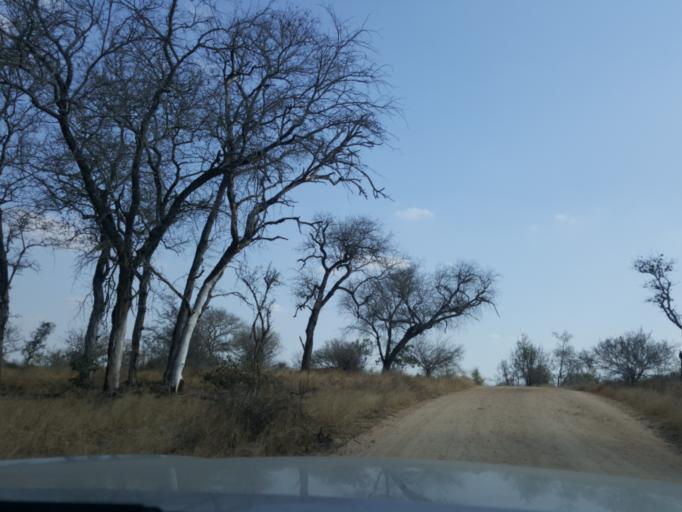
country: ZA
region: Mpumalanga
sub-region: Ehlanzeni District
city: Komatipoort
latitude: -25.2827
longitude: 31.7719
